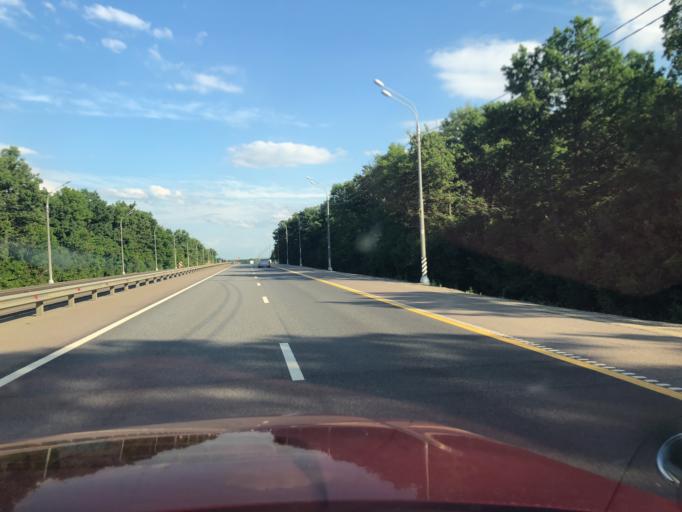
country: RU
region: Lipetsk
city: Zadonsk
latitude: 52.4162
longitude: 38.8418
